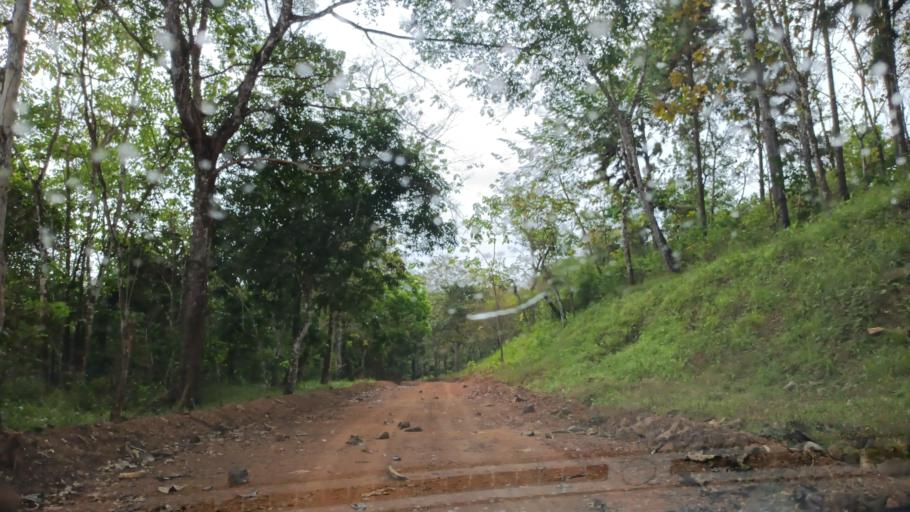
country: PA
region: Panama
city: La Cabima
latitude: 9.1279
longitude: -79.5105
